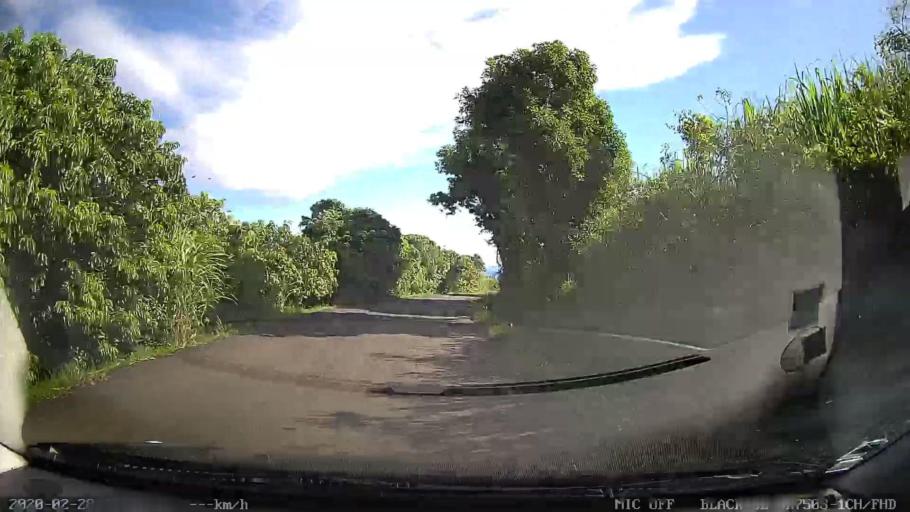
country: RE
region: Reunion
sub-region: Reunion
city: Sainte-Marie
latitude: -20.9371
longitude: 55.5259
